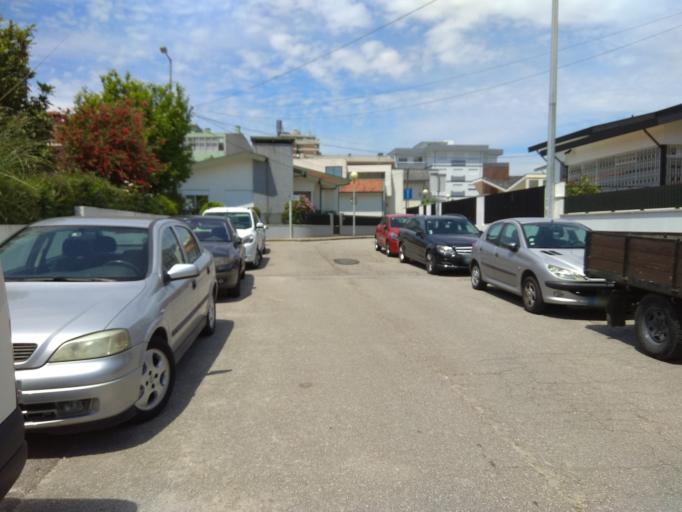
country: PT
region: Porto
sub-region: Maia
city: Maia
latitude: 41.2290
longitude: -8.6214
